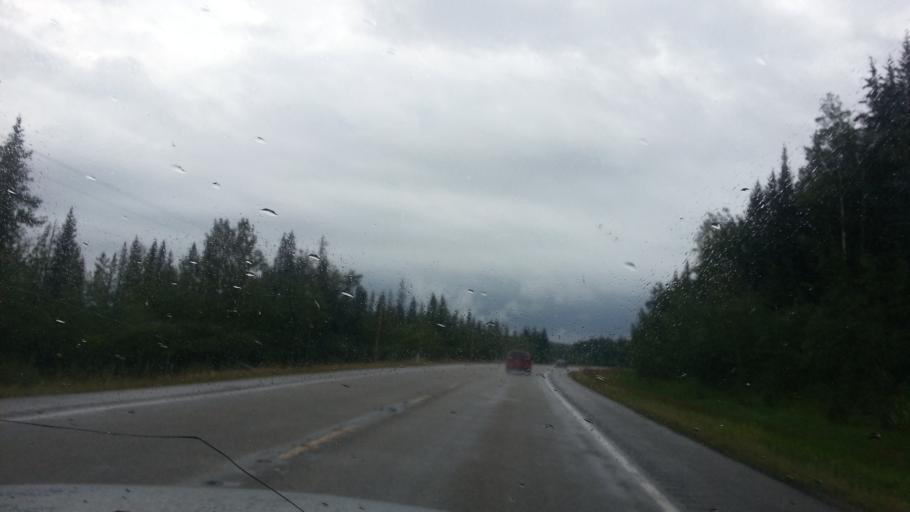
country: CA
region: Alberta
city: Cochrane
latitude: 50.9165
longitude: -114.6152
